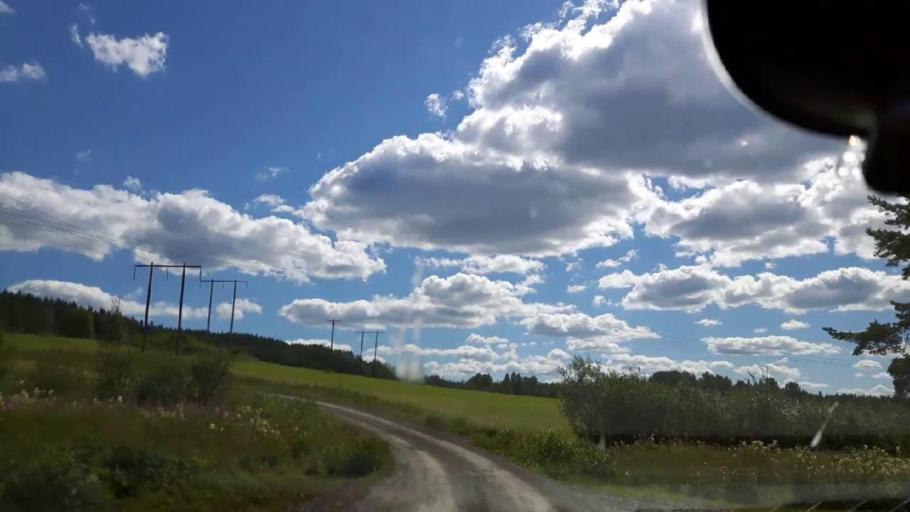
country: SE
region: Jaemtland
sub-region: Ragunda Kommun
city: Hammarstrand
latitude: 62.9555
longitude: 16.6788
